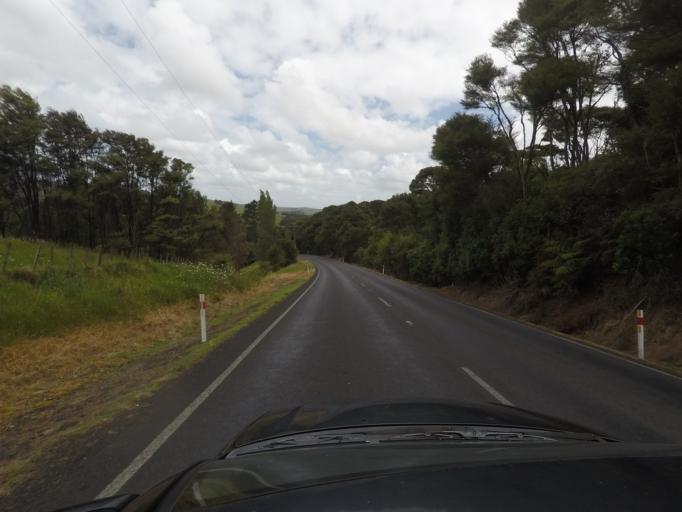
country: NZ
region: Auckland
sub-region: Auckland
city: Parakai
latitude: -36.5453
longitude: 174.4629
